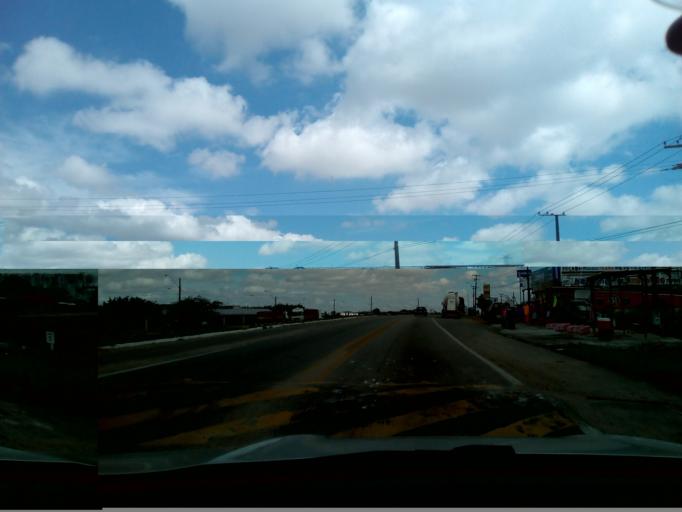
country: BR
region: Paraiba
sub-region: Campina Grande
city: Campina Grande
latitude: -7.2787
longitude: -35.8954
